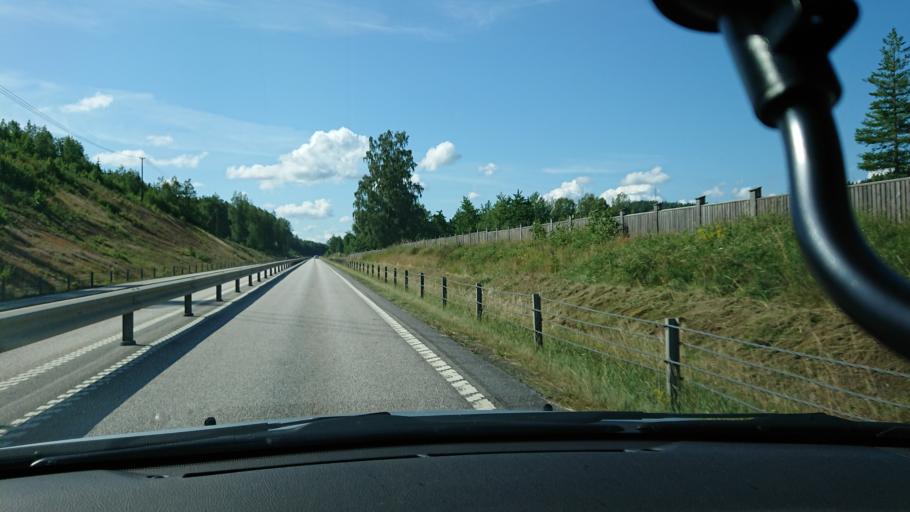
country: SE
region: OEstergoetland
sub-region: Kinda Kommun
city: Kisa
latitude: 58.0277
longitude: 15.6571
